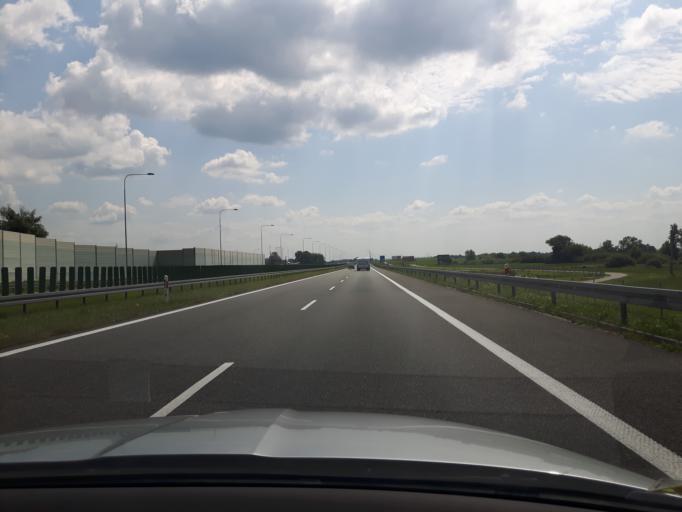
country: PL
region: Warmian-Masurian Voivodeship
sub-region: Powiat ostrodzki
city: Milomlyn
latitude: 53.8099
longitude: 19.7843
